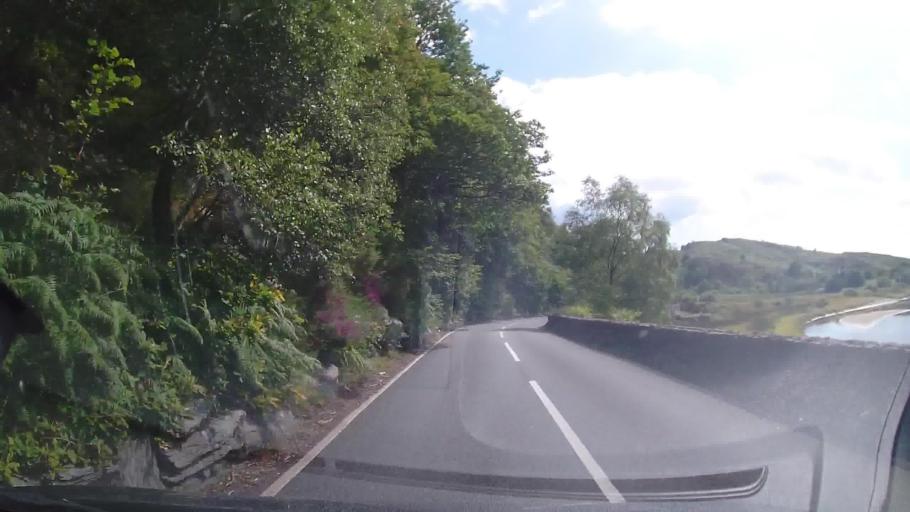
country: GB
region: Wales
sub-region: Gwynedd
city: Penrhyndeudraeth
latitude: 52.9271
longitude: -4.0435
